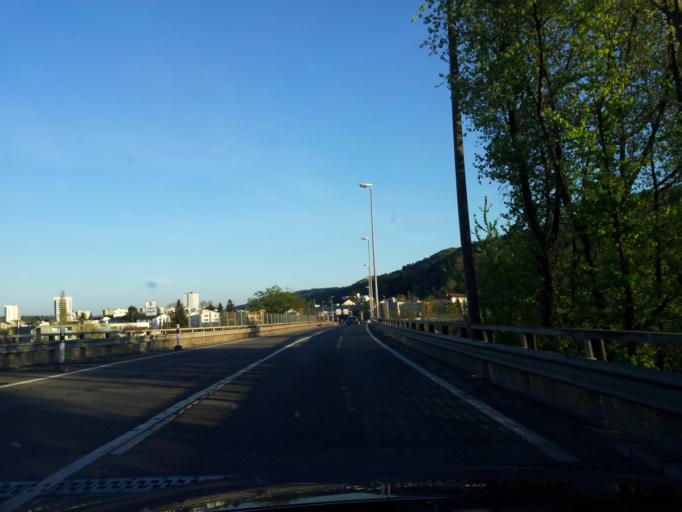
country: CH
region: Aargau
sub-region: Bezirk Baden
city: Neuenhof
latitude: 47.4571
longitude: 8.3185
